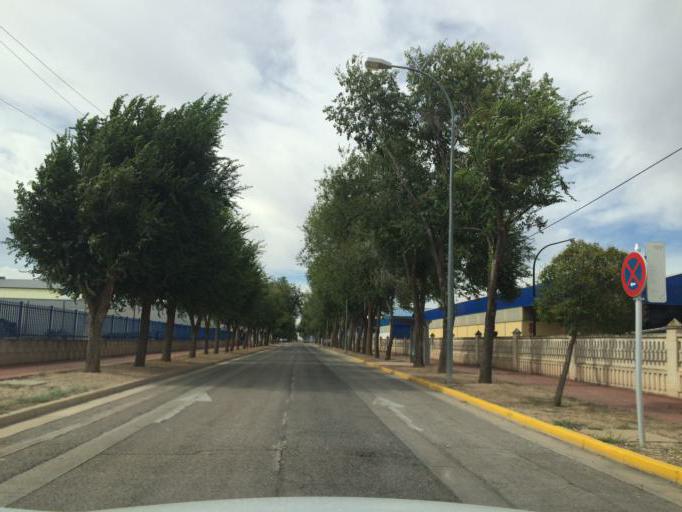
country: ES
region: Castille-La Mancha
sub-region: Provincia de Albacete
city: Albacete
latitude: 39.0170
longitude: -1.8846
